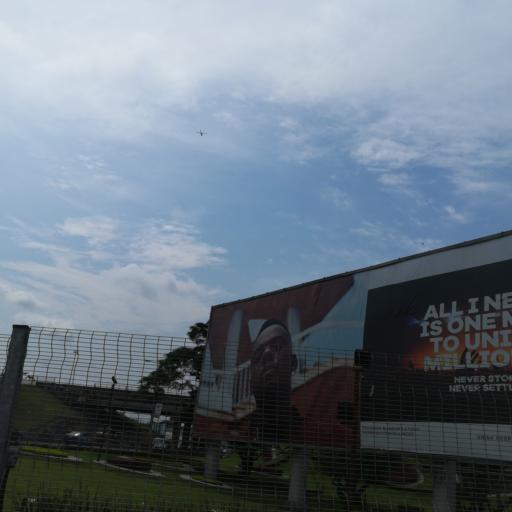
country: NG
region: Rivers
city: Port Harcourt
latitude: 4.8368
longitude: 7.0152
